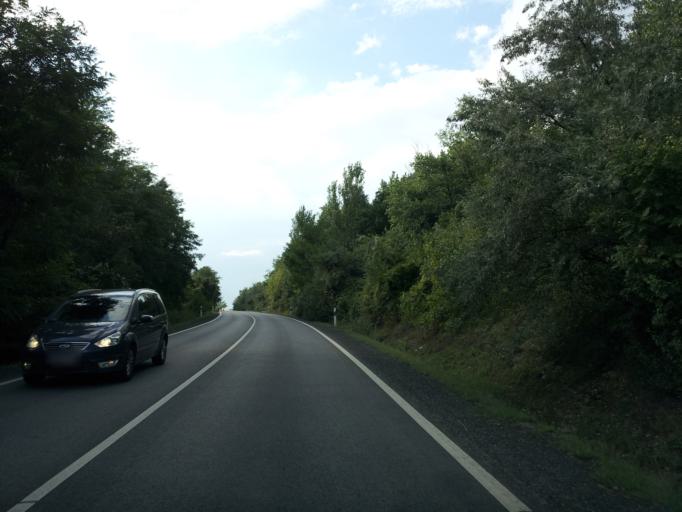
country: HU
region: Pest
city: Vac
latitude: 47.8036
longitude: 19.1032
